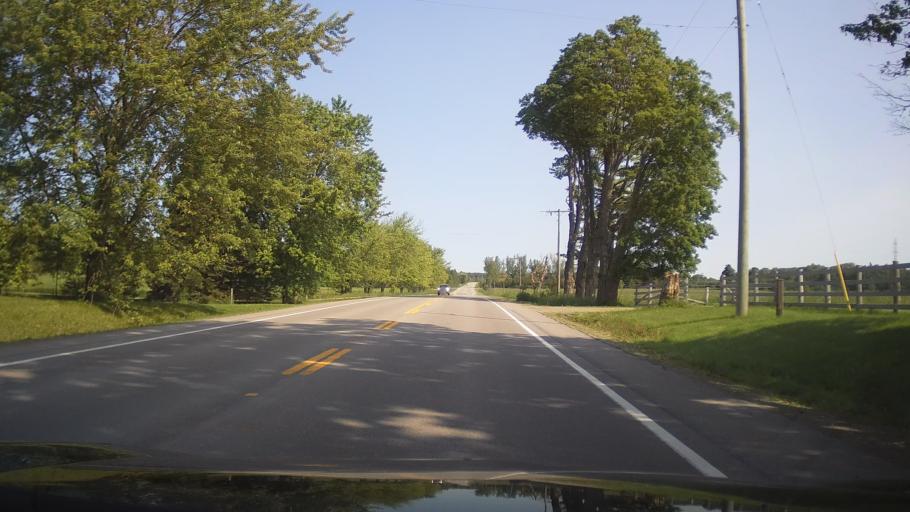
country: CA
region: Ontario
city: Omemee
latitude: 44.3994
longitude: -78.9093
